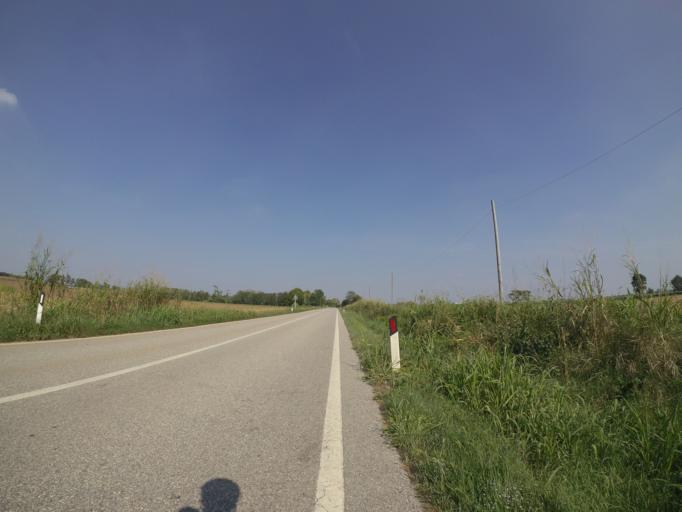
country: IT
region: Friuli Venezia Giulia
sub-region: Provincia di Udine
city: Basiliano
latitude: 46.0053
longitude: 13.0499
